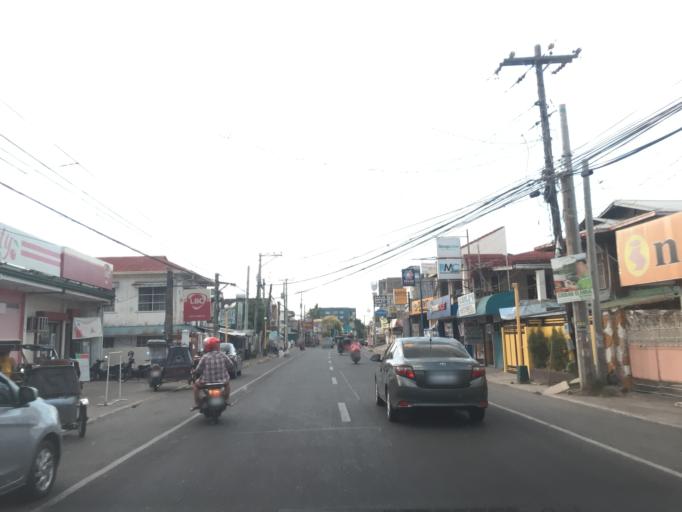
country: PH
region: Ilocos
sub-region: Province of Pangasinan
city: Bolingit
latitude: 15.9285
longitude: 120.3482
